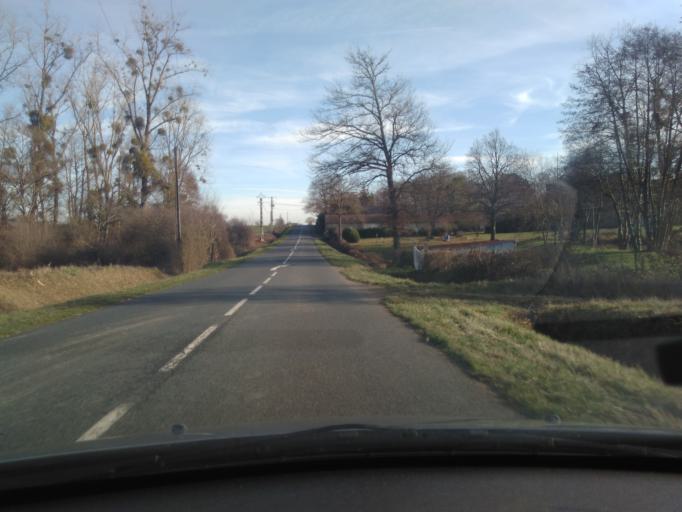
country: FR
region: Centre
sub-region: Departement du Cher
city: Le Chatelet
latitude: 46.6417
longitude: 2.2551
